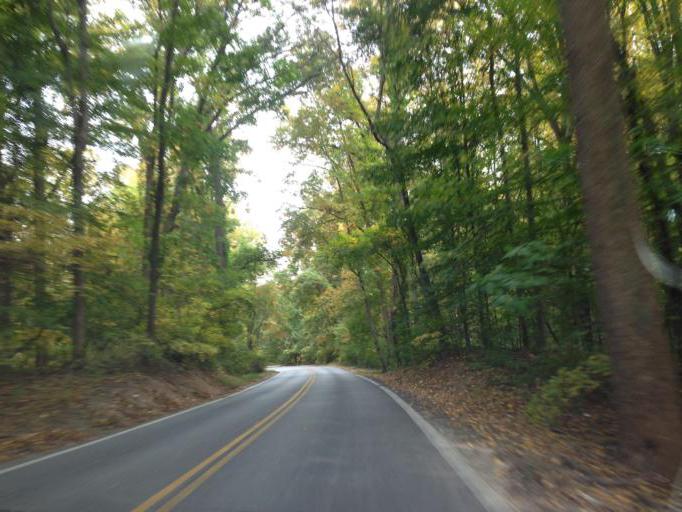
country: US
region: Maryland
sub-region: Howard County
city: Ellicott City
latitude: 39.3094
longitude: -76.7959
